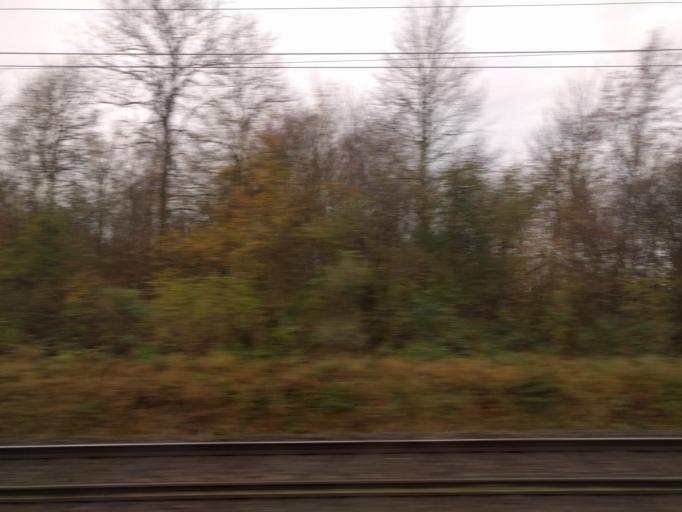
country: DK
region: Zealand
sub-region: Roskilde Kommune
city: Roskilde
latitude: 55.6154
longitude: 12.0505
